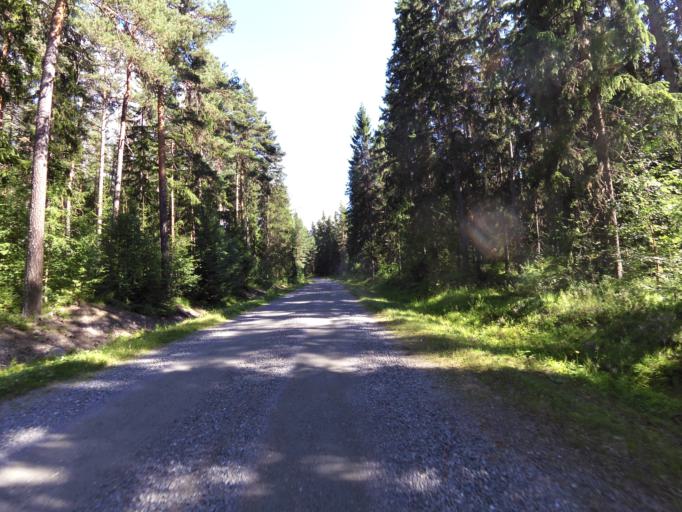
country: SE
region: Dalarna
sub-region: Faluns Kommun
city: Svardsjo
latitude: 60.6609
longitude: 15.8619
